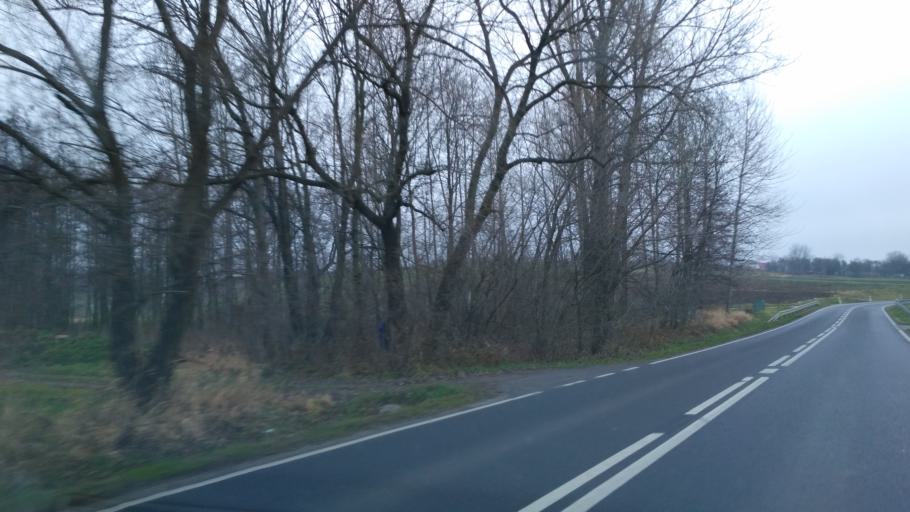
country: PL
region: Subcarpathian Voivodeship
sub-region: Powiat jaroslawski
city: Pruchnik
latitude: 49.9111
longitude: 22.5577
